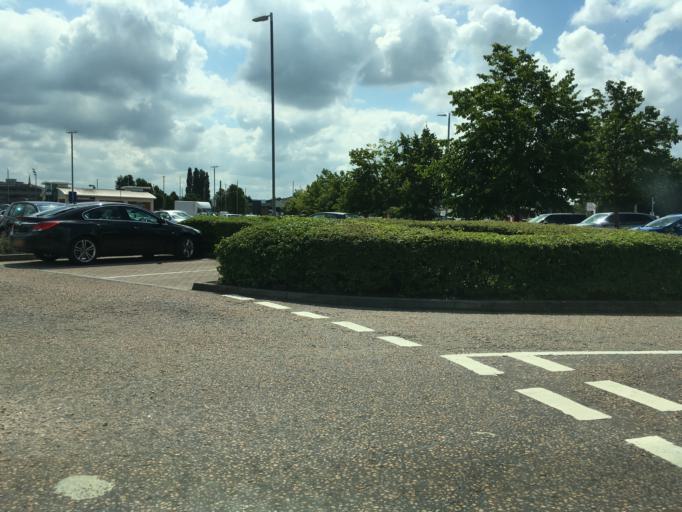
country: GB
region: England
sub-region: Gloucestershire
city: Gloucester
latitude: 51.8743
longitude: -2.2479
